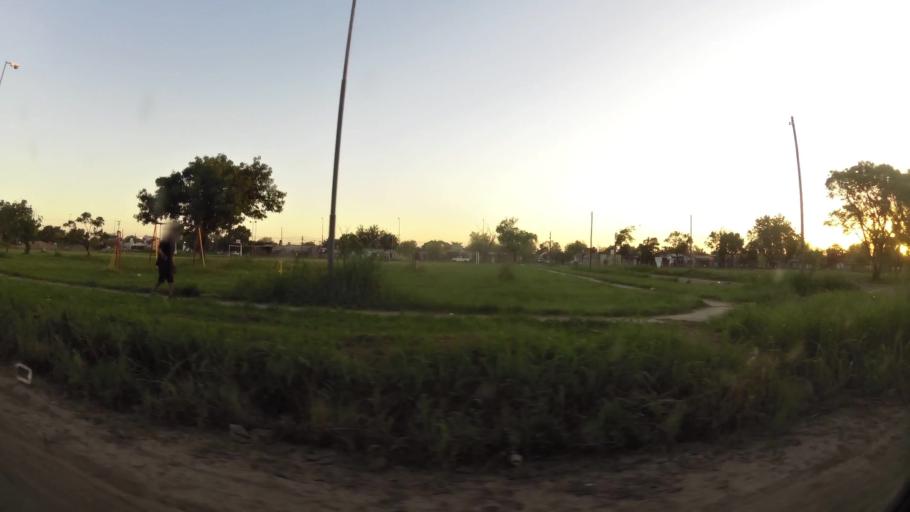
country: AR
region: Santa Fe
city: Santa Fe de la Vera Cruz
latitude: -31.5924
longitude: -60.6963
